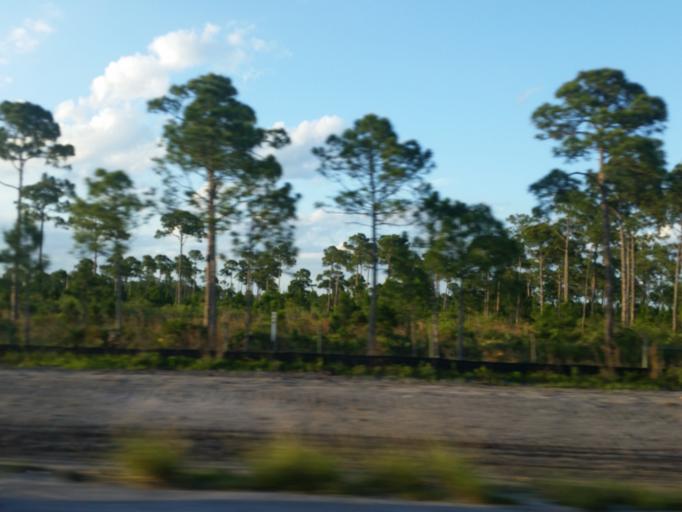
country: US
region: Florida
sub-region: Sarasota County
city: Warm Mineral Springs
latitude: 27.1018
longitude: -82.2863
